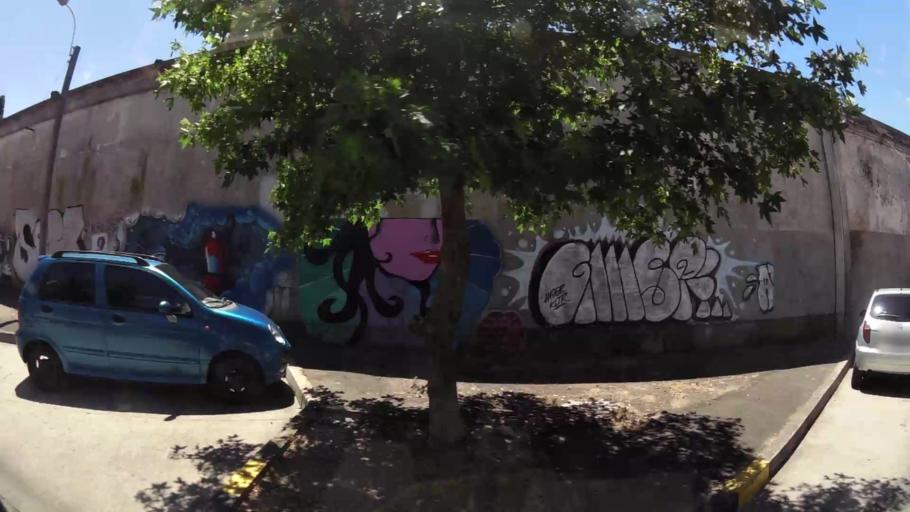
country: UY
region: Montevideo
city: Montevideo
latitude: -34.9021
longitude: -56.1271
